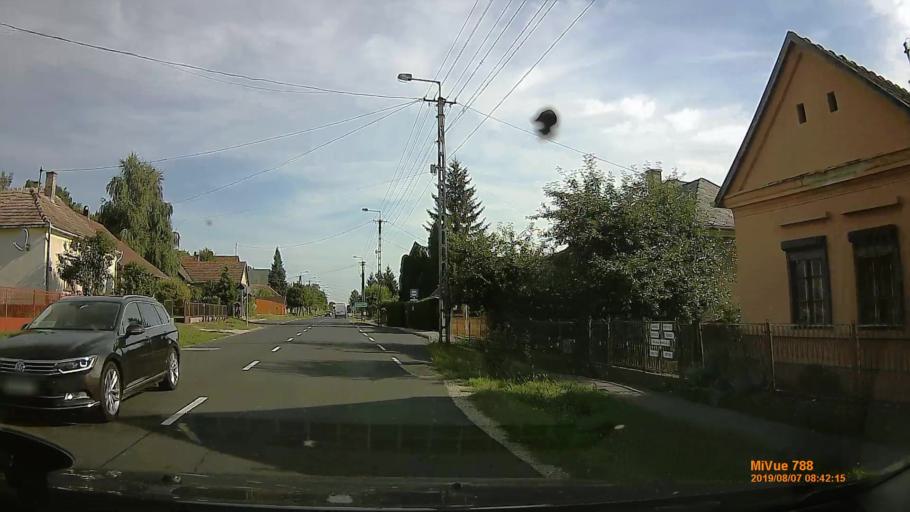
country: HU
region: Zala
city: Pacsa
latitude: 46.5976
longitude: 16.9184
